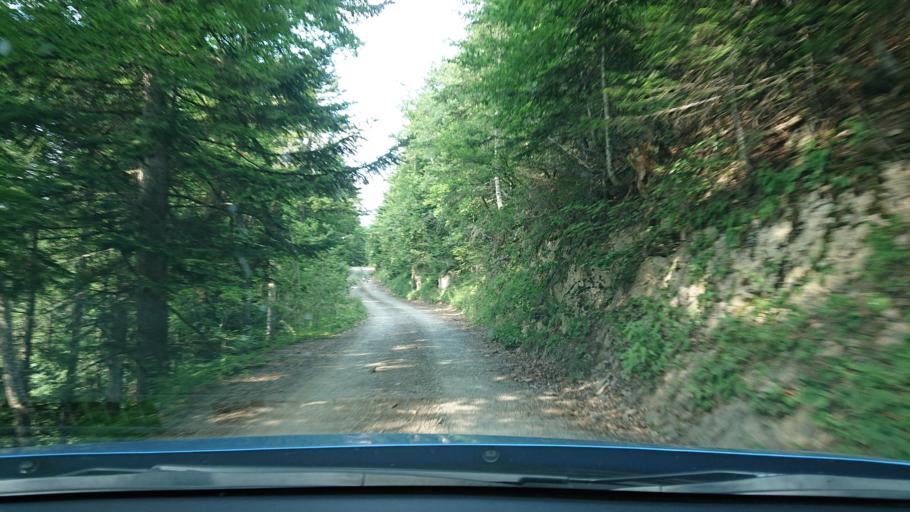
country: FR
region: Rhone-Alpes
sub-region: Departement de l'Isere
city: Mens
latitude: 44.7872
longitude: 5.8805
